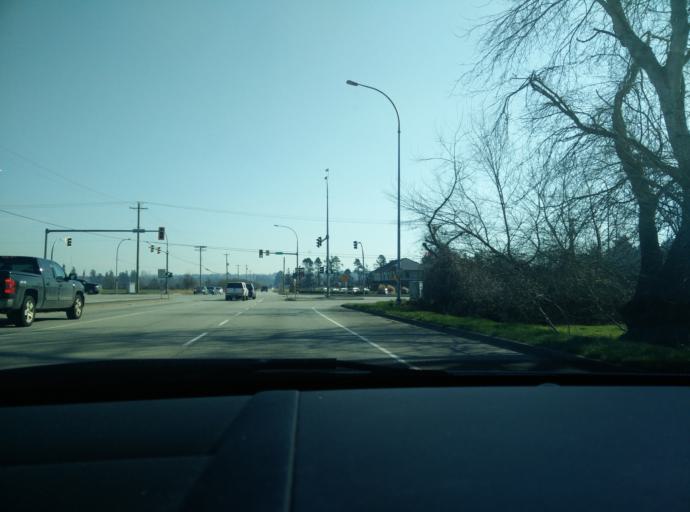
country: US
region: Washington
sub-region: Whatcom County
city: Blaine
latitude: 49.0166
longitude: -122.7364
